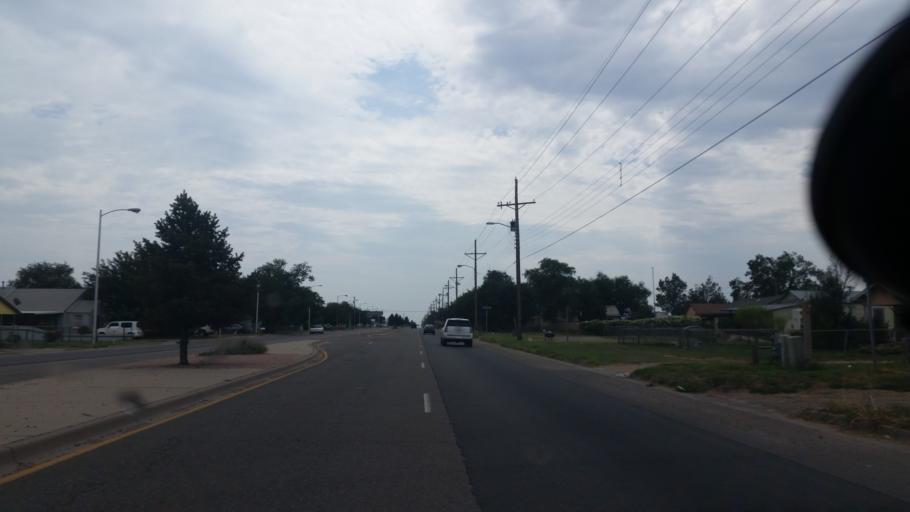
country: US
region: New Mexico
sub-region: Curry County
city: Clovis
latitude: 34.3870
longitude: -103.1966
